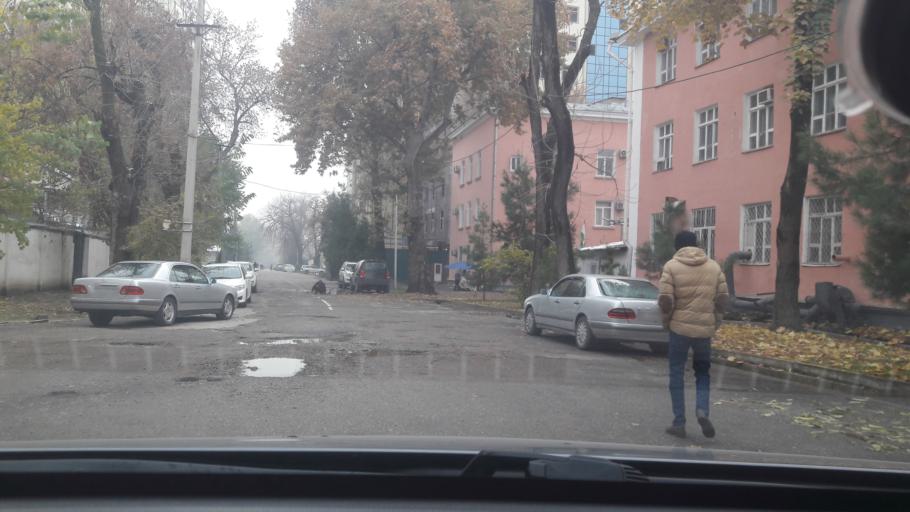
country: TJ
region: Dushanbe
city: Dushanbe
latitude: 38.5753
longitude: 68.7947
